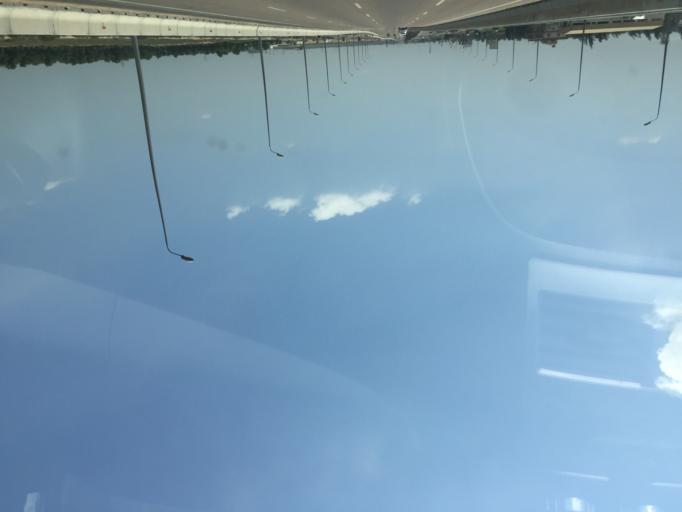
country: EG
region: Al Buhayrah
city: Abu al Matamir
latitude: 30.7037
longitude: 30.0459
